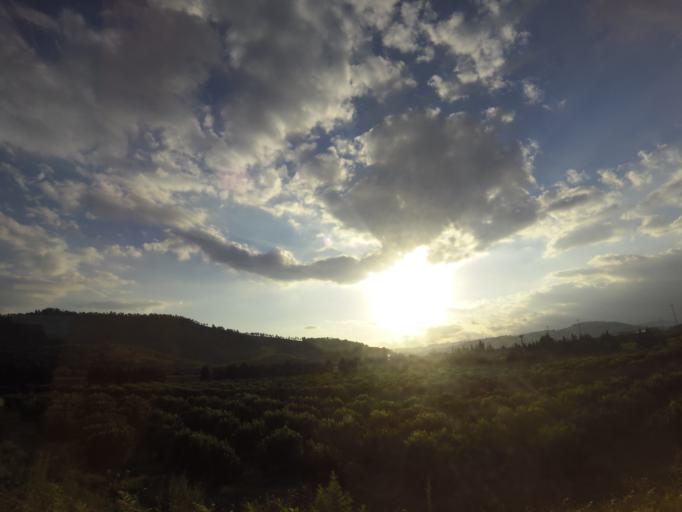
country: IT
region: Calabria
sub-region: Provincia di Catanzaro
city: Catanzaro
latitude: 38.8521
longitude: 16.5766
